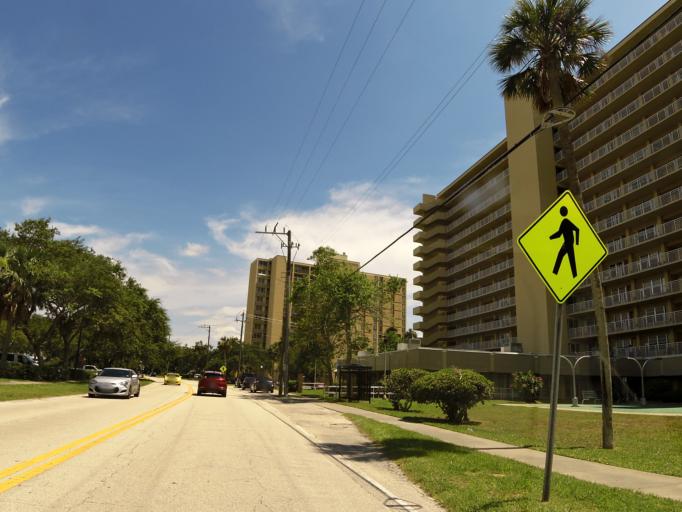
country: US
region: Florida
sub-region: Volusia County
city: Daytona Beach
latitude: 29.2033
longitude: -81.0155
